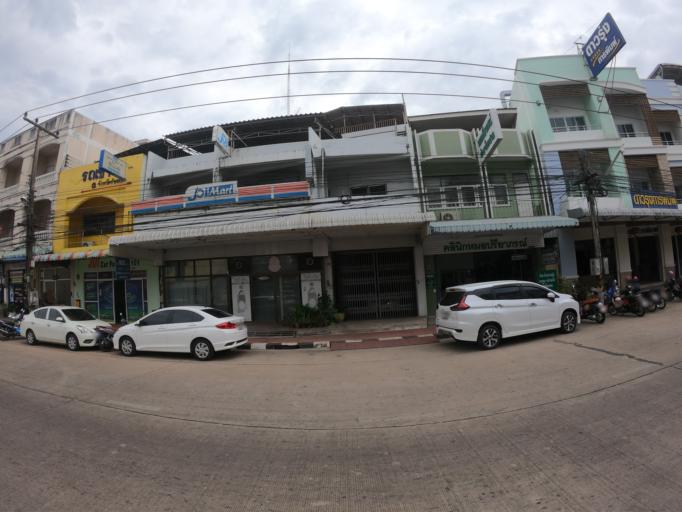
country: TH
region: Roi Et
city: Roi Et
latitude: 16.0606
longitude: 103.6577
